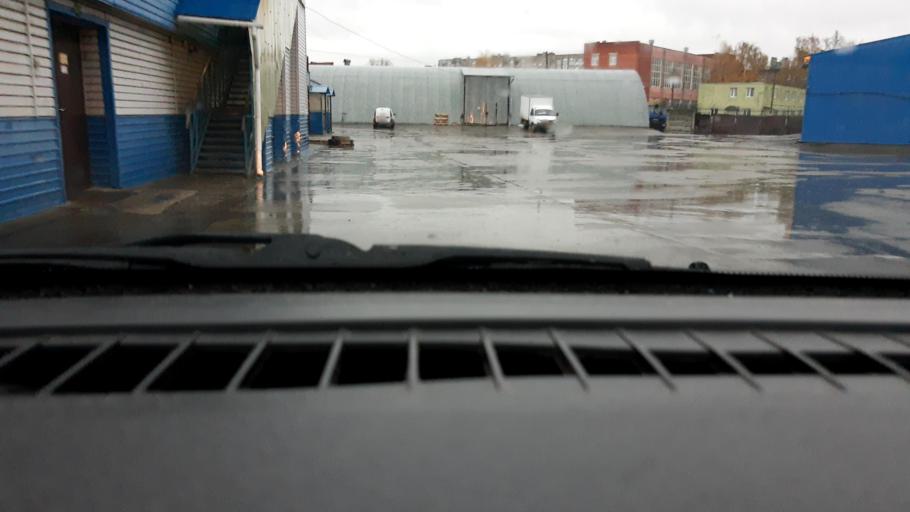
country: RU
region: Nizjnij Novgorod
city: Gorbatovka
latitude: 56.2536
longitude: 43.8754
